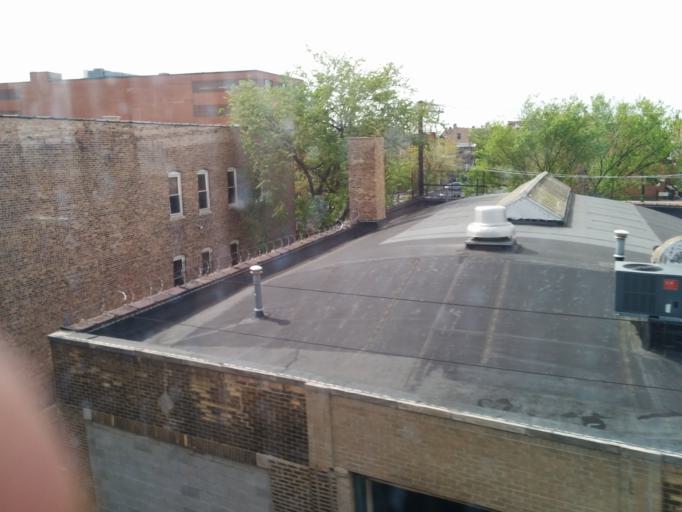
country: US
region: Illinois
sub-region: Cook County
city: Cicero
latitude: 41.8842
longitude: -87.7076
